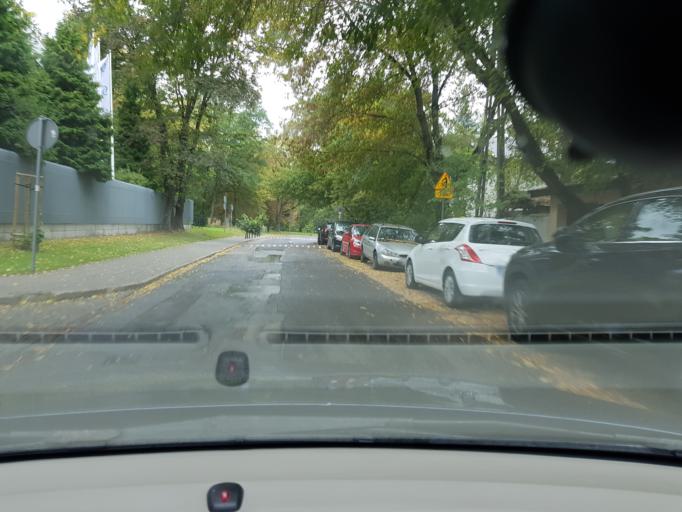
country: PL
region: Masovian Voivodeship
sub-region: Warszawa
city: Zoliborz
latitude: 52.2769
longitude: 20.9699
